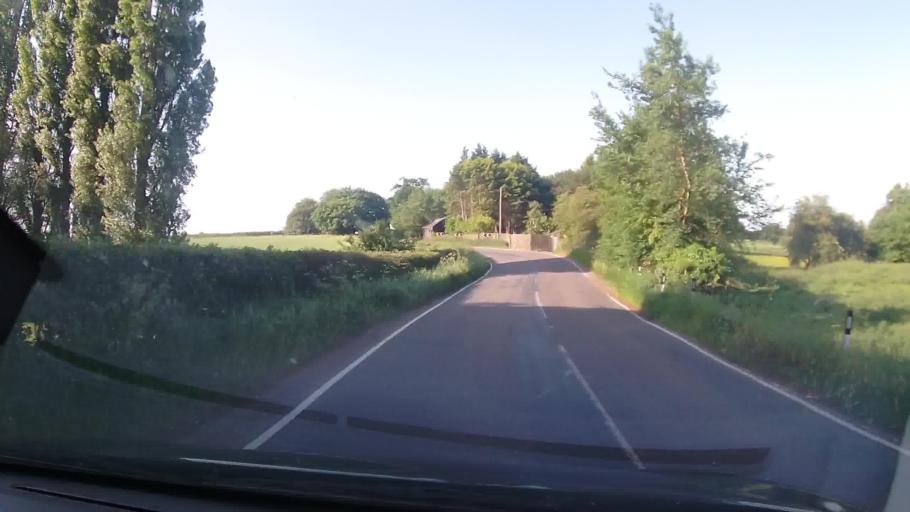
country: GB
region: England
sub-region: Shropshire
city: Shawbury
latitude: 52.7679
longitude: -2.6339
